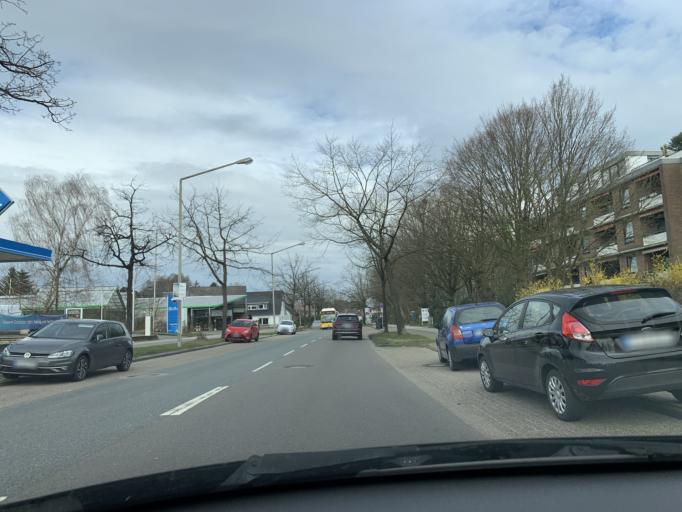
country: DE
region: Lower Saxony
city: Oldenburg
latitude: 53.1257
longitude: 8.1905
